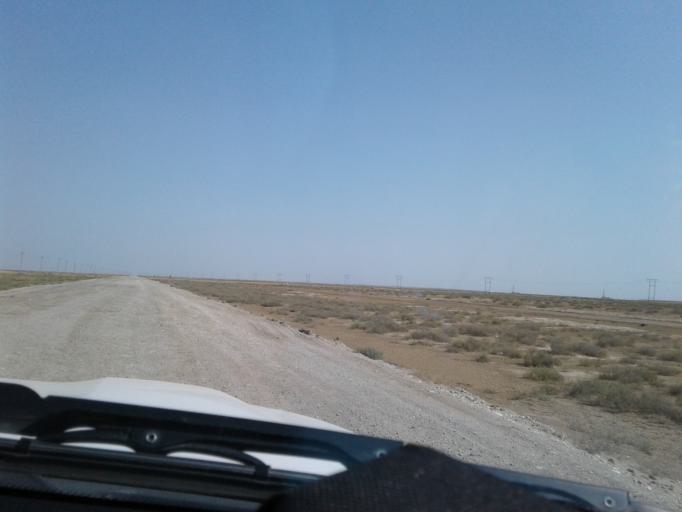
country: IR
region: Golestan
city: Gomishan
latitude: 37.7835
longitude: 53.9166
